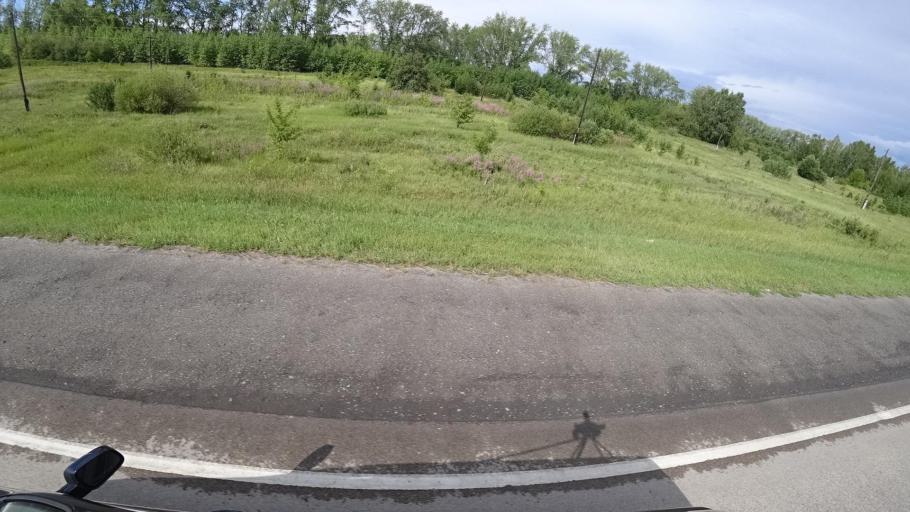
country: RU
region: Sverdlovsk
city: Kamyshlov
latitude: 56.8432
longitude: 62.7763
